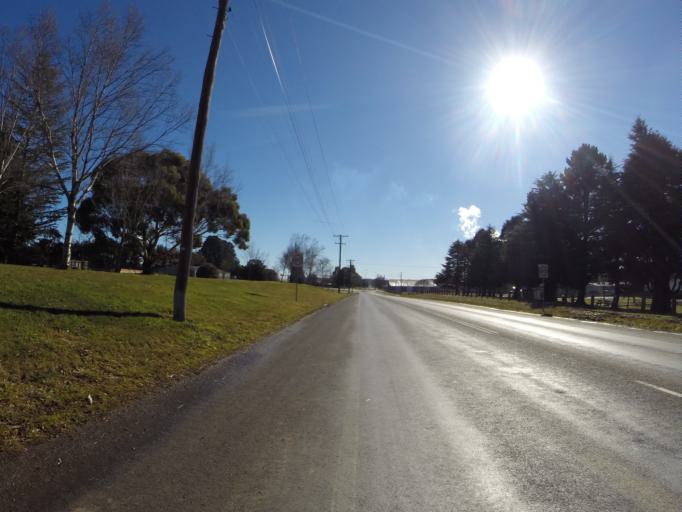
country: AU
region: New South Wales
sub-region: Oberon
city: Oberon
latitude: -33.7007
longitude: 149.8547
